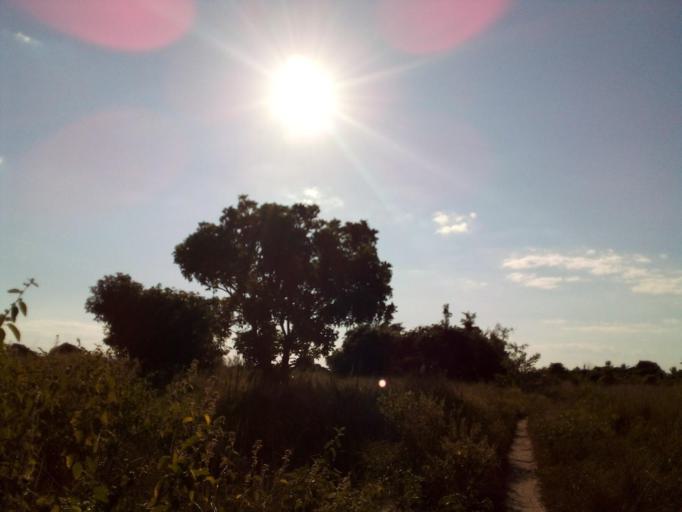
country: MZ
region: Zambezia
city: Quelimane
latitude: -17.5118
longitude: 36.6836
